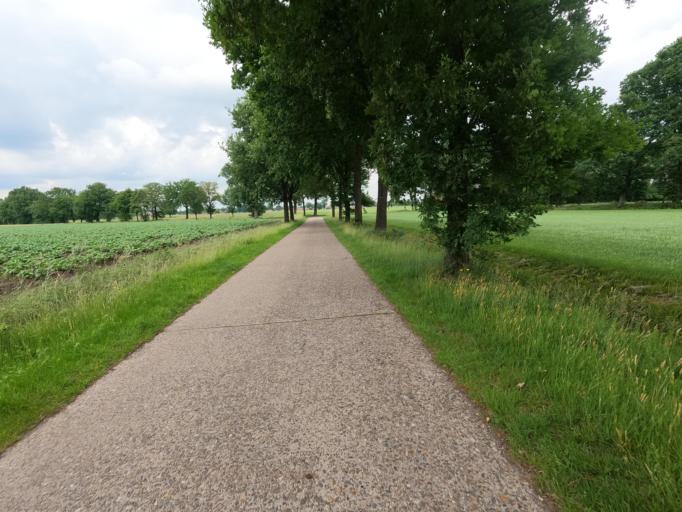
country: BE
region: Flanders
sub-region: Provincie Antwerpen
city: Kalmthout
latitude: 51.3790
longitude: 4.4972
